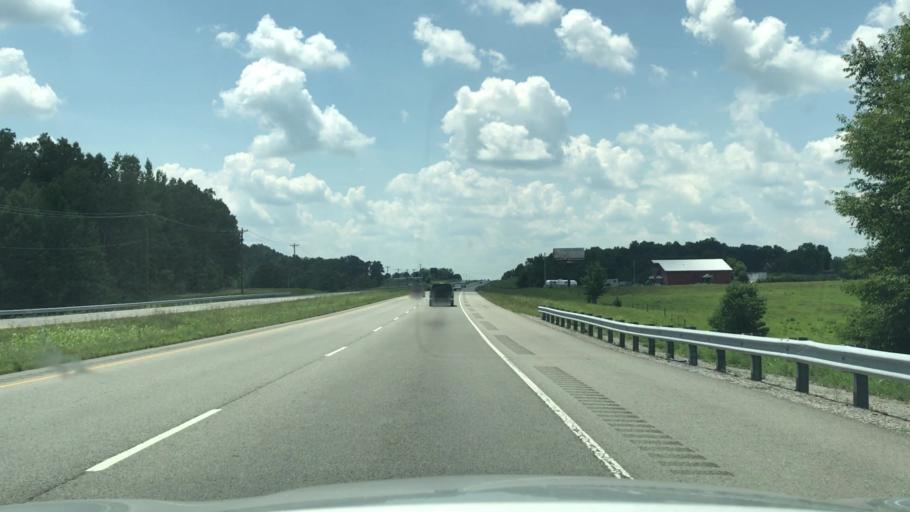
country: US
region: Tennessee
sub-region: Overton County
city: Livingston
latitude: 36.3070
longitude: -85.3665
